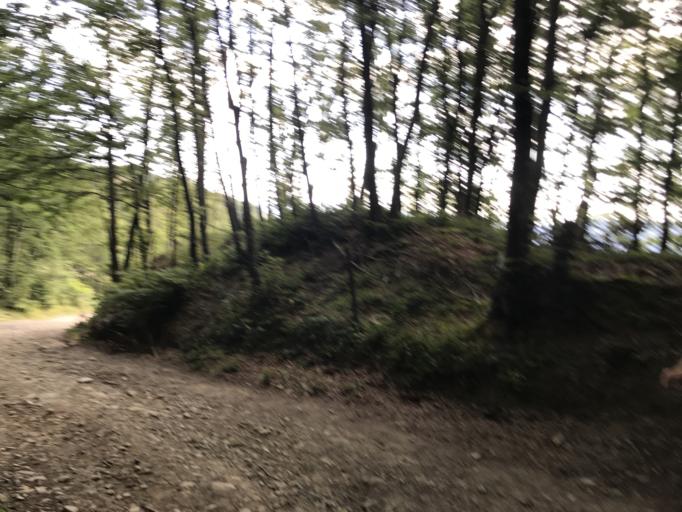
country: IT
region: Emilia-Romagna
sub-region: Provincia di Bologna
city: San Benedetto Val di Sambro
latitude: 44.1549
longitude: 11.2622
